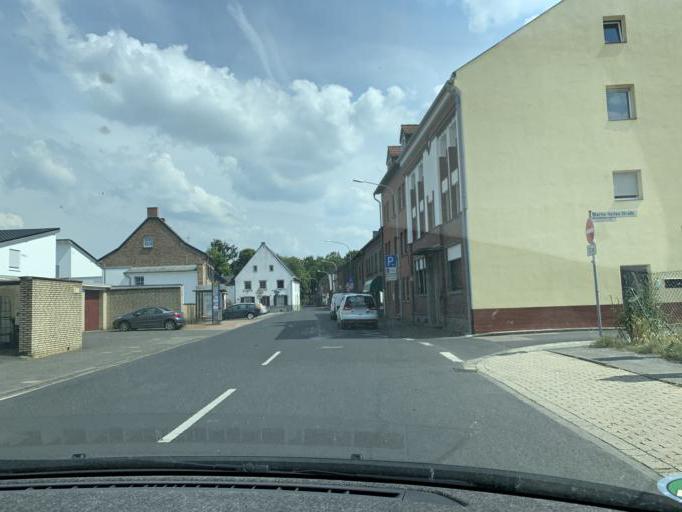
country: DE
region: North Rhine-Westphalia
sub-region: Regierungsbezirk Koln
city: Bedburg
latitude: 50.9718
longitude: 6.5927
